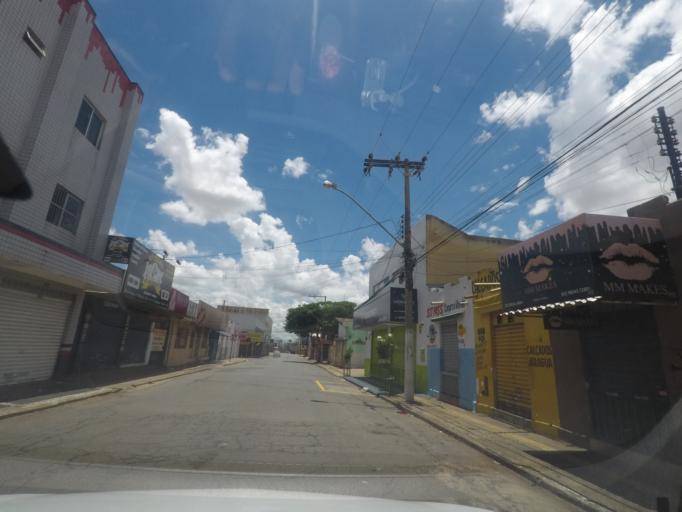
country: BR
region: Goias
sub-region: Goiania
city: Goiania
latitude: -16.6726
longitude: -49.2943
